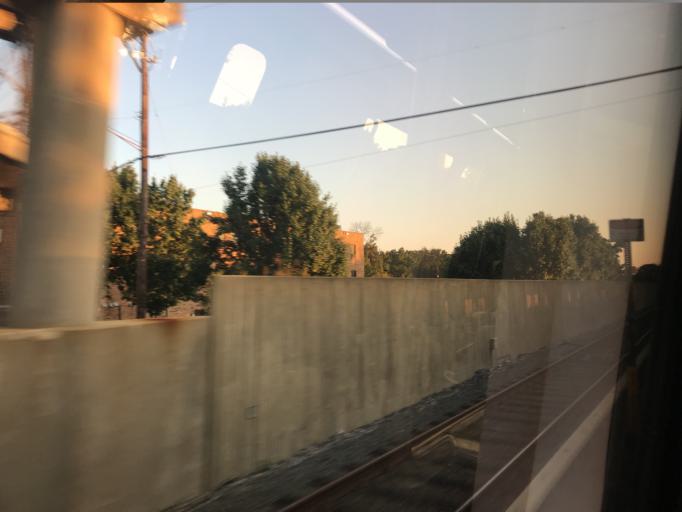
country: US
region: Maryland
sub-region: Prince George's County
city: Berwyn Heights
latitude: 38.9943
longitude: -76.9217
